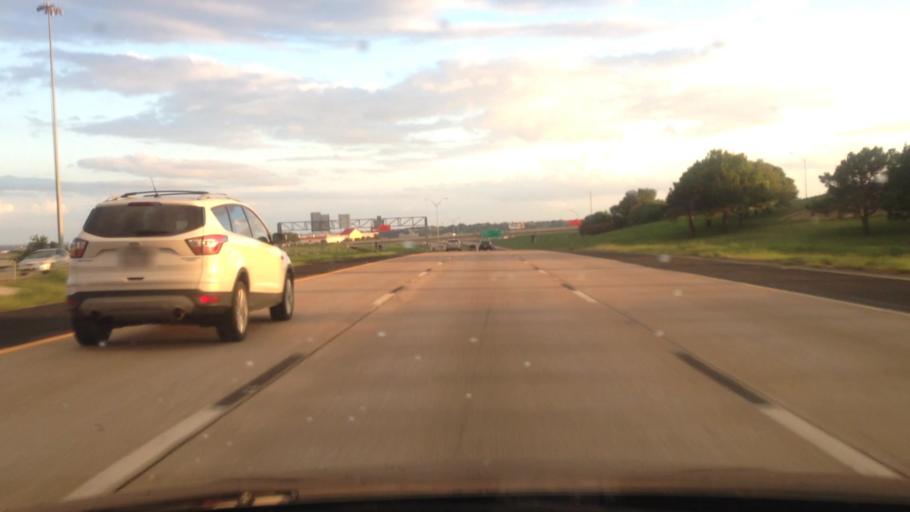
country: US
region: Texas
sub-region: Tarrant County
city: White Settlement
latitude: 32.7374
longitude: -97.4815
